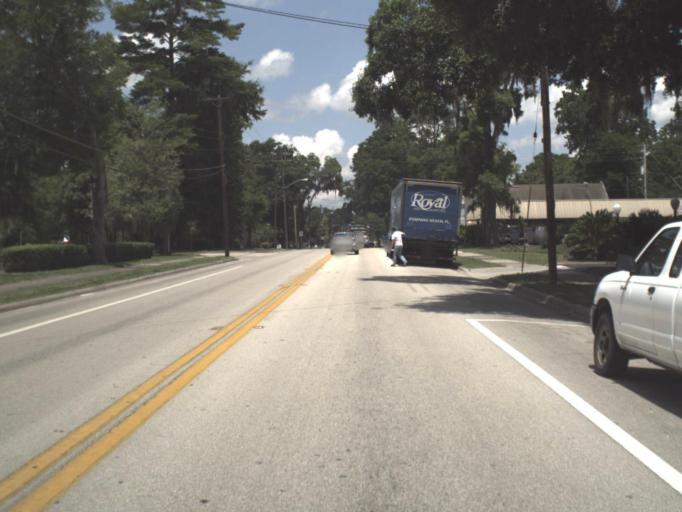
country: US
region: Florida
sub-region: Alachua County
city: High Springs
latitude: 29.8256
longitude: -82.5936
